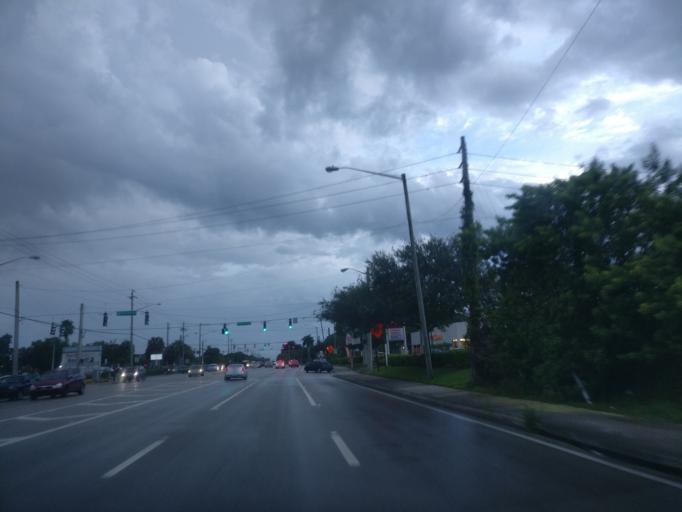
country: US
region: Florida
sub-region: Palm Beach County
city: Schall Circle
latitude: 26.7090
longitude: -80.1194
